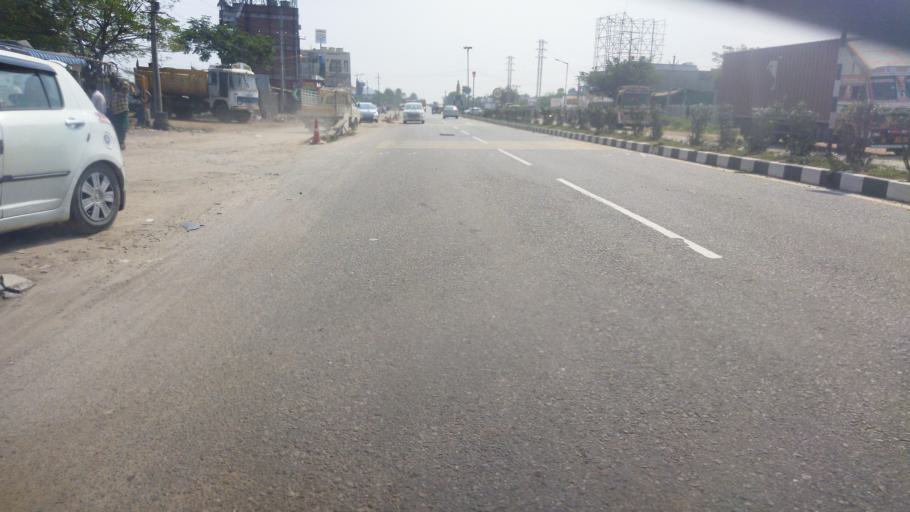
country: IN
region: Telangana
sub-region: Nalgonda
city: Nalgonda
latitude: 17.0744
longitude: 79.2847
